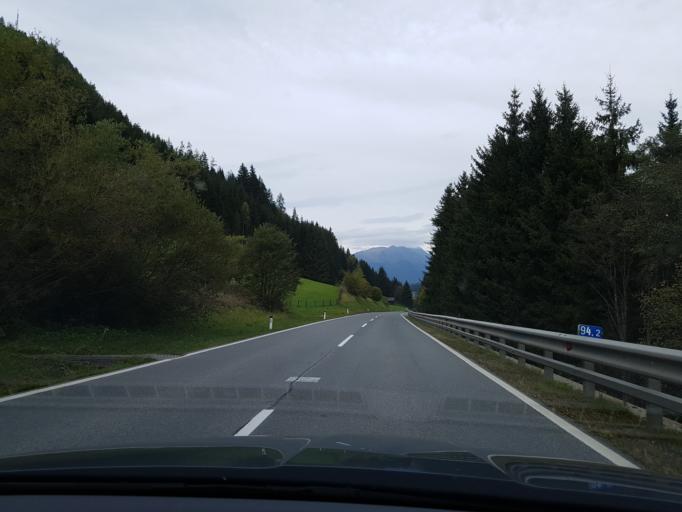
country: AT
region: Salzburg
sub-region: Politischer Bezirk Tamsweg
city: Tamsweg
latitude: 47.1146
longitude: 13.8146
